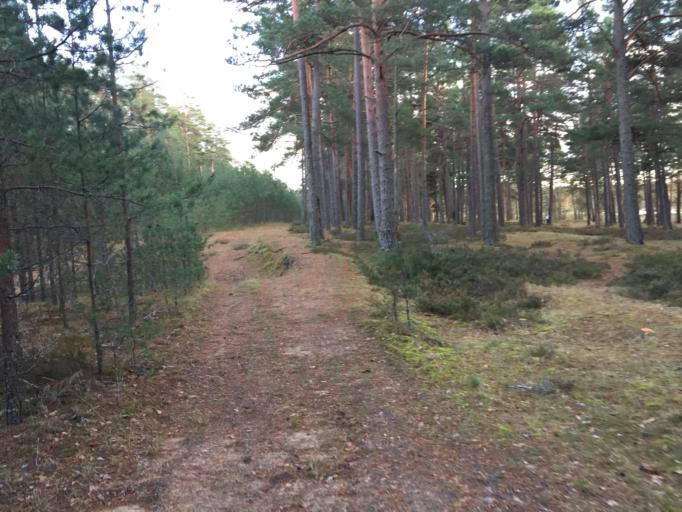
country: LV
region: Carnikava
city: Carnikava
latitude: 57.1716
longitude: 24.3317
